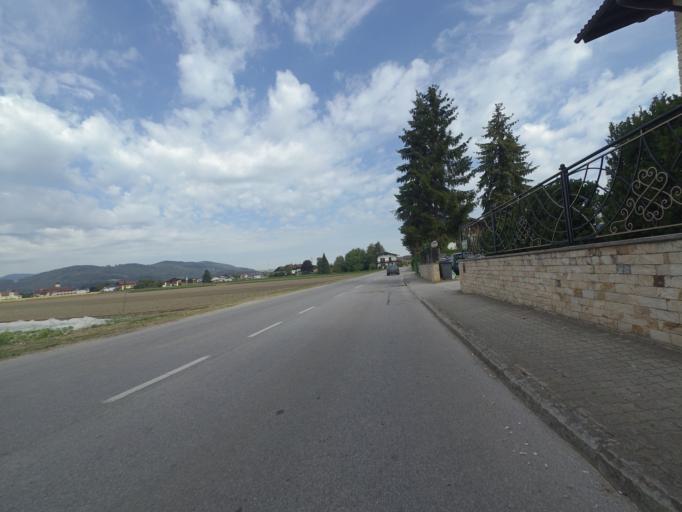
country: DE
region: Bavaria
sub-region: Upper Bavaria
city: Ainring
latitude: 47.7858
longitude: 12.9741
